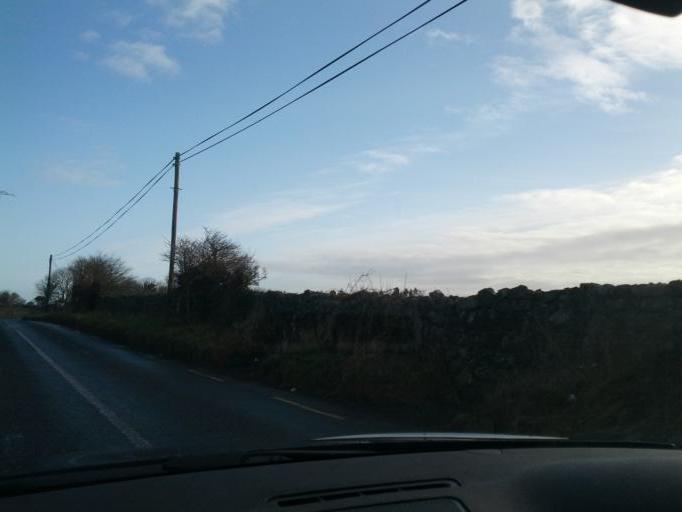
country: IE
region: Connaught
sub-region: County Galway
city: Athenry
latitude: 53.3822
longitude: -8.6945
